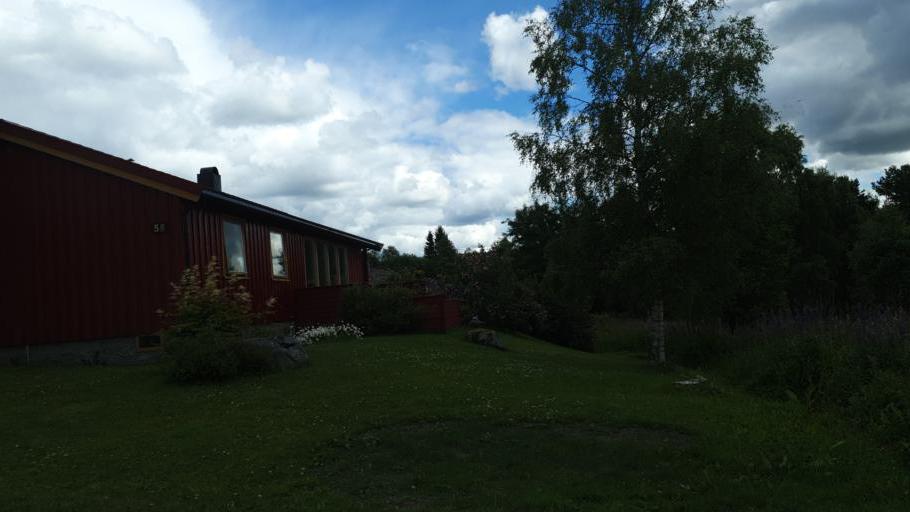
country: NO
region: Sor-Trondelag
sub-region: Rennebu
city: Berkak
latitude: 62.8311
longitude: 10.0037
